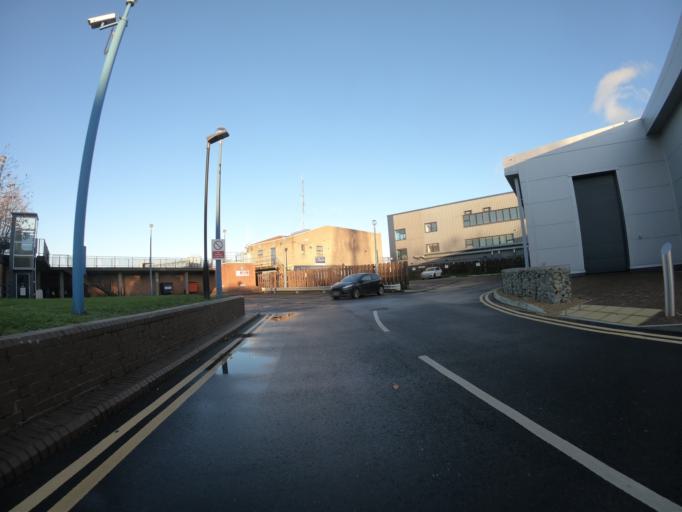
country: GB
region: England
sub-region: Greater London
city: Woolwich
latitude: 51.4951
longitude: 0.0413
